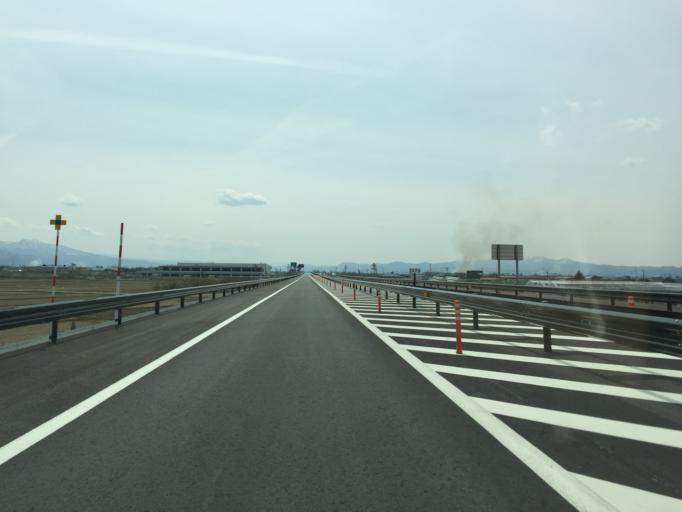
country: JP
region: Yamagata
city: Higashine
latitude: 38.4175
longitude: 140.3500
